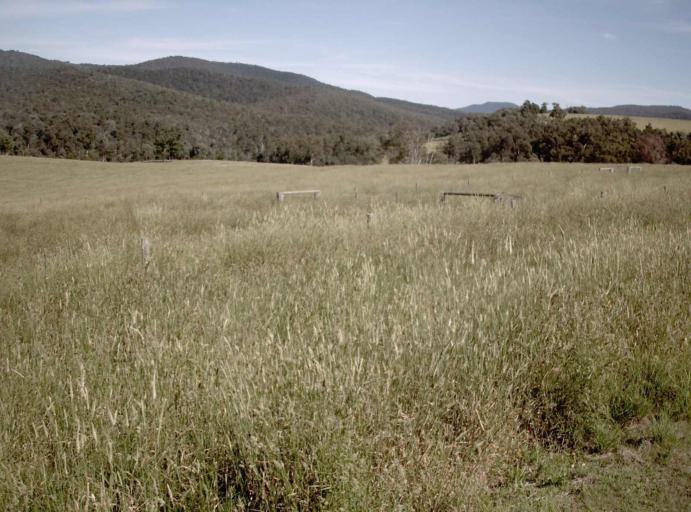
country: AU
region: Victoria
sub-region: East Gippsland
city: Lakes Entrance
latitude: -37.5018
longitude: 148.1329
